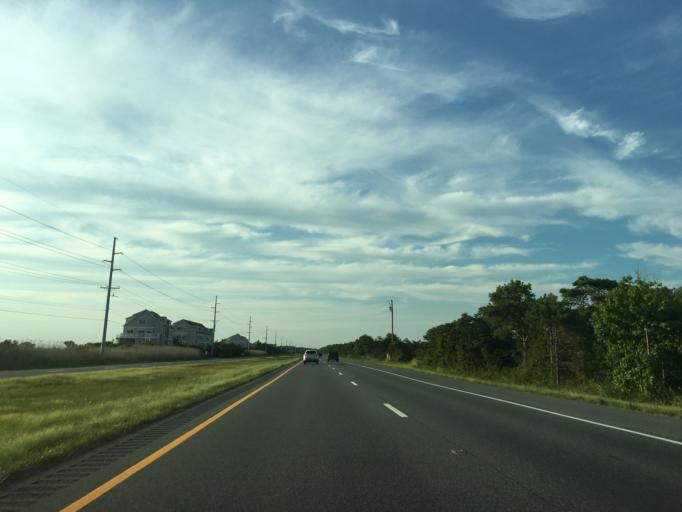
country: US
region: Delaware
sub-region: Sussex County
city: Bethany Beach
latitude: 38.4868
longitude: -75.0529
